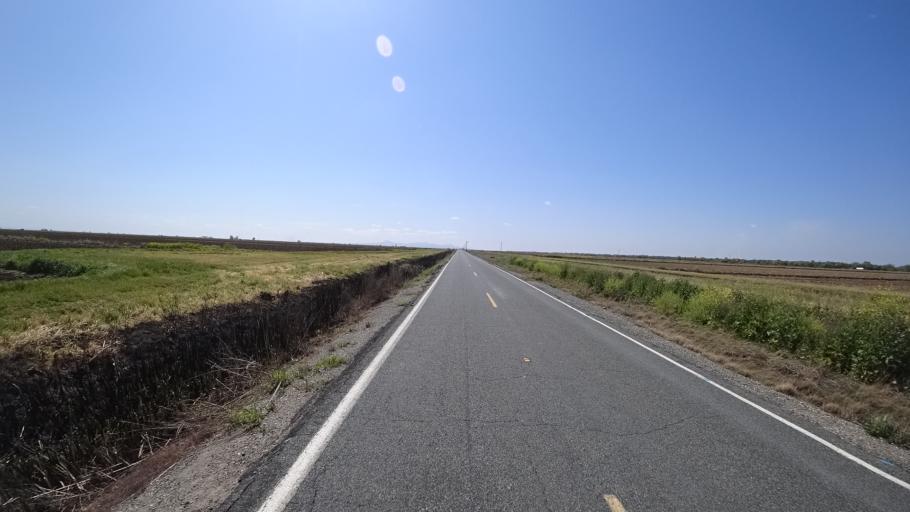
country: US
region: California
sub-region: Butte County
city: Durham
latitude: 39.5126
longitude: -121.8574
